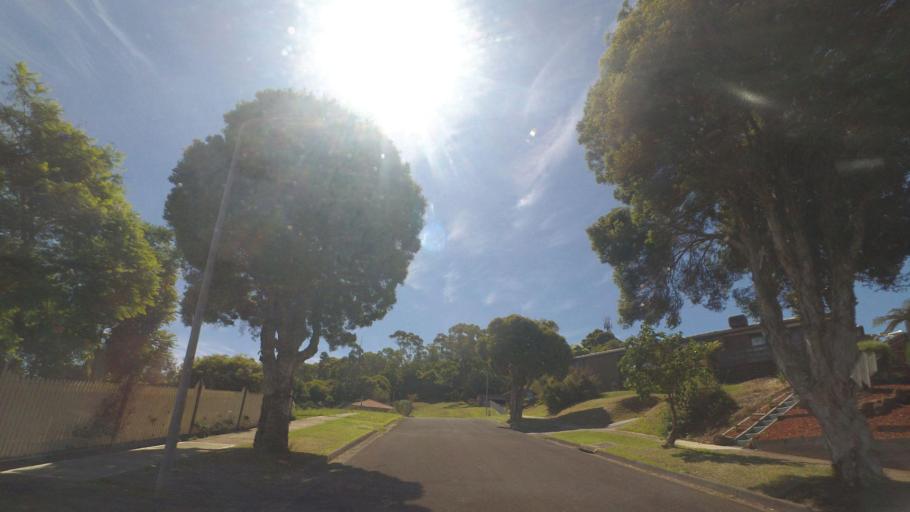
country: AU
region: Victoria
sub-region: Yarra Ranges
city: Lilydale
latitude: -37.7637
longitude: 145.3274
